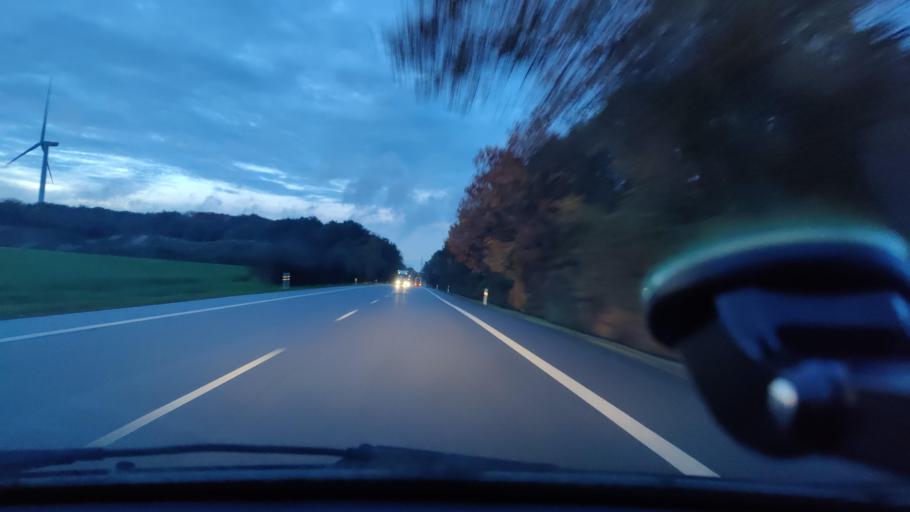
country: DE
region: North Rhine-Westphalia
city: Straelen
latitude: 51.3958
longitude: 6.2644
